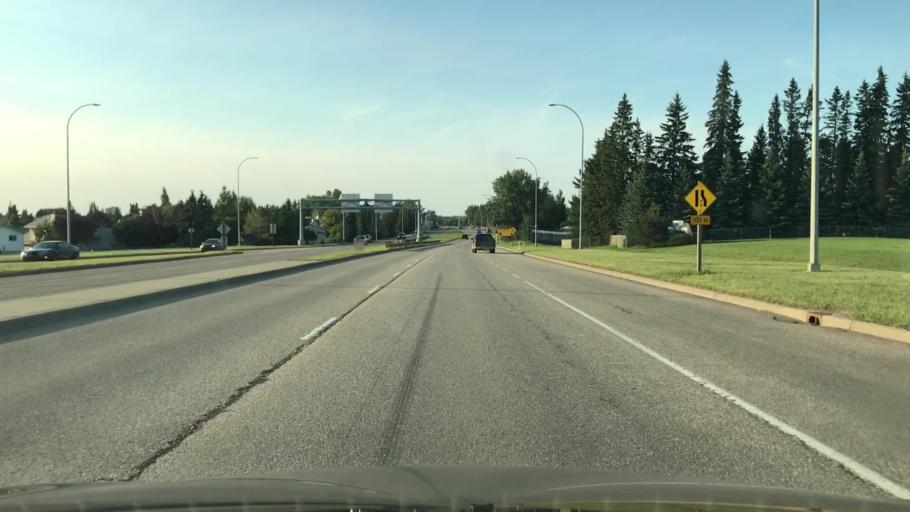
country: CA
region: Alberta
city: Beaumont
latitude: 53.4382
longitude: -113.4181
